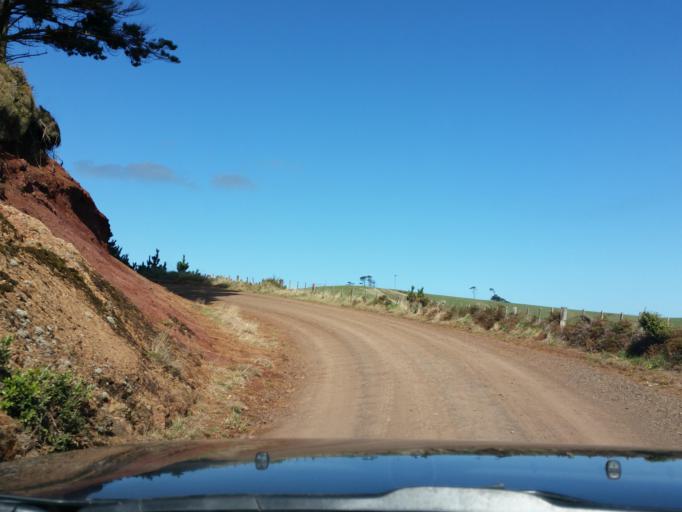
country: NZ
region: Northland
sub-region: Kaipara District
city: Dargaville
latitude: -35.7262
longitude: 173.5710
